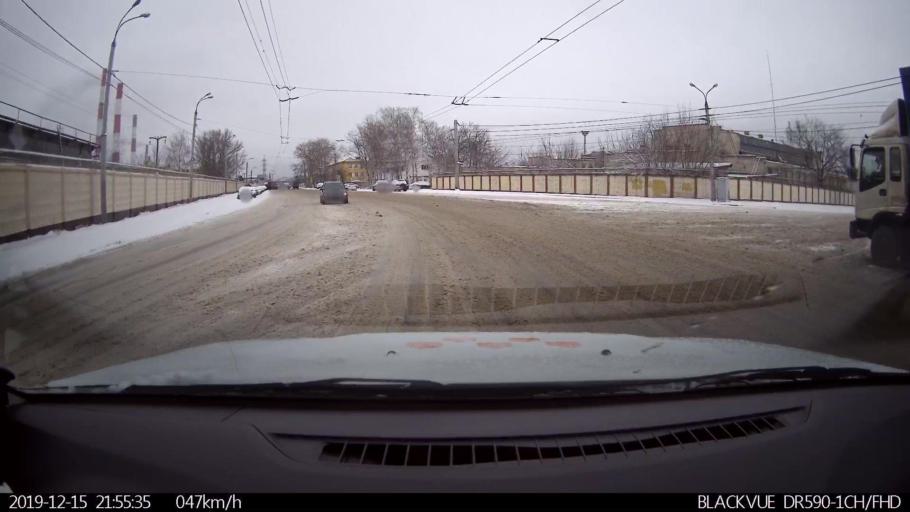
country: RU
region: Nizjnij Novgorod
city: Burevestnik
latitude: 56.2367
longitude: 43.8846
